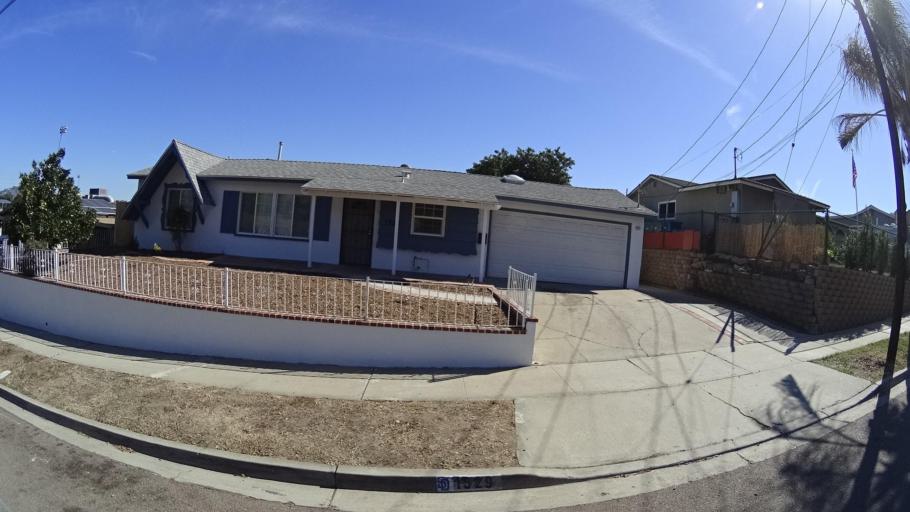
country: US
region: California
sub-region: San Diego County
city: Lemon Grove
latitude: 32.7217
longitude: -117.0193
